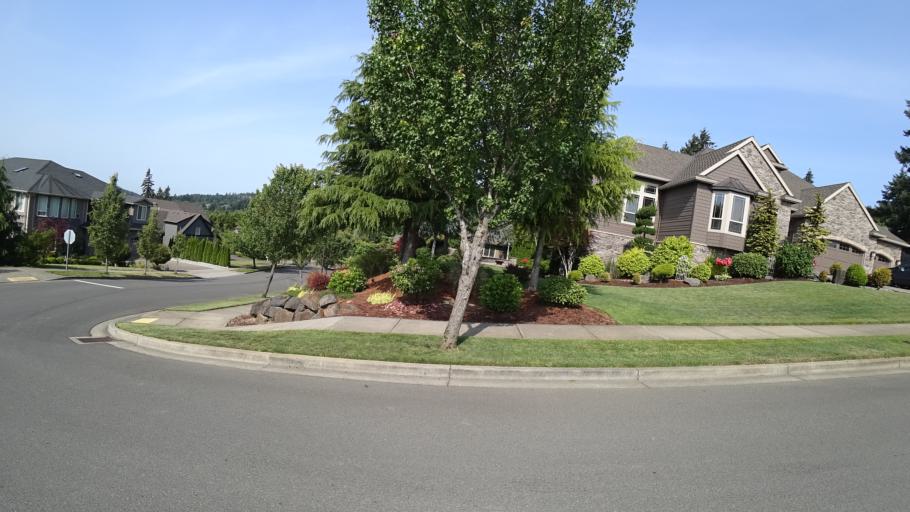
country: US
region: Oregon
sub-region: Clackamas County
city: Happy Valley
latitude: 45.4563
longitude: -122.5204
